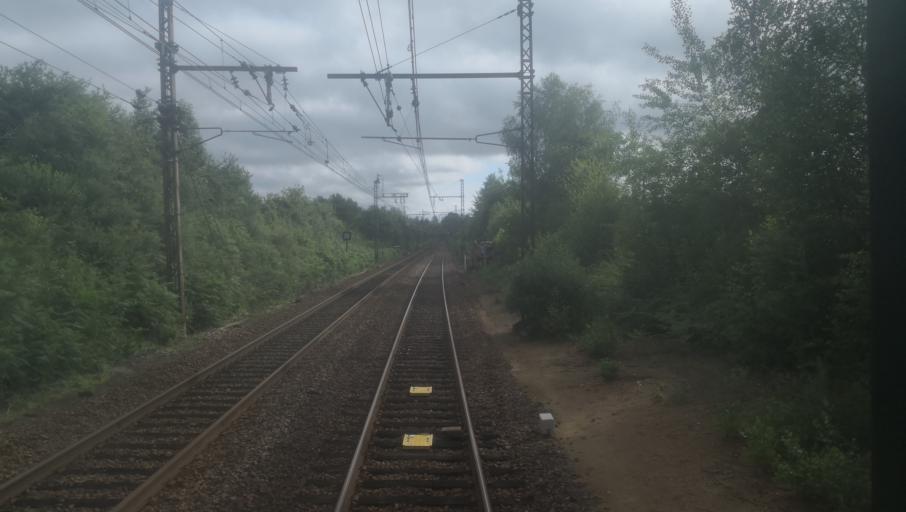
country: FR
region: Limousin
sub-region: Departement de la Haute-Vienne
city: Le Palais-sur-Vienne
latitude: 45.8582
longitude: 1.3091
